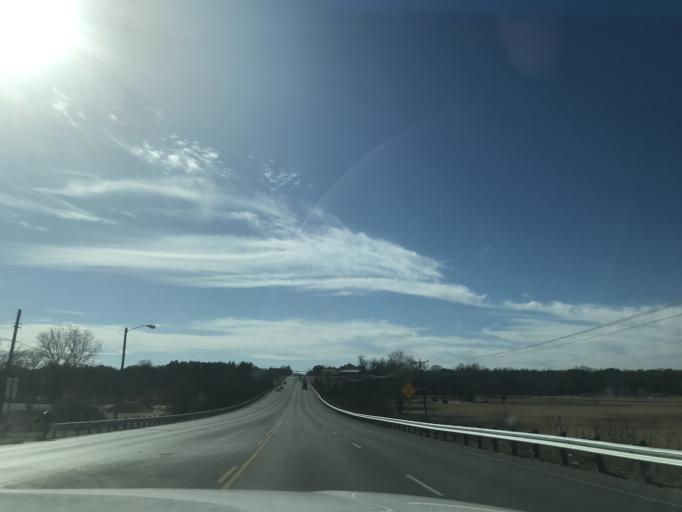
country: US
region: Texas
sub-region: Erath County
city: Stephenville
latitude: 32.2106
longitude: -98.1985
